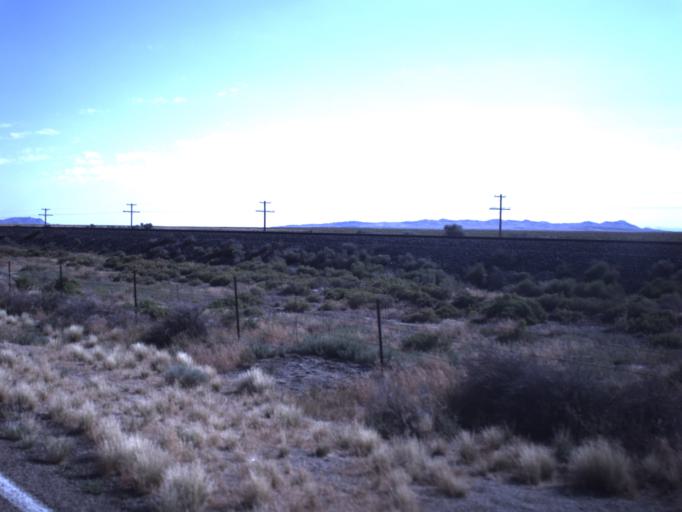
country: US
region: Utah
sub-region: Beaver County
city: Milford
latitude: 38.6387
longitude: -112.9835
